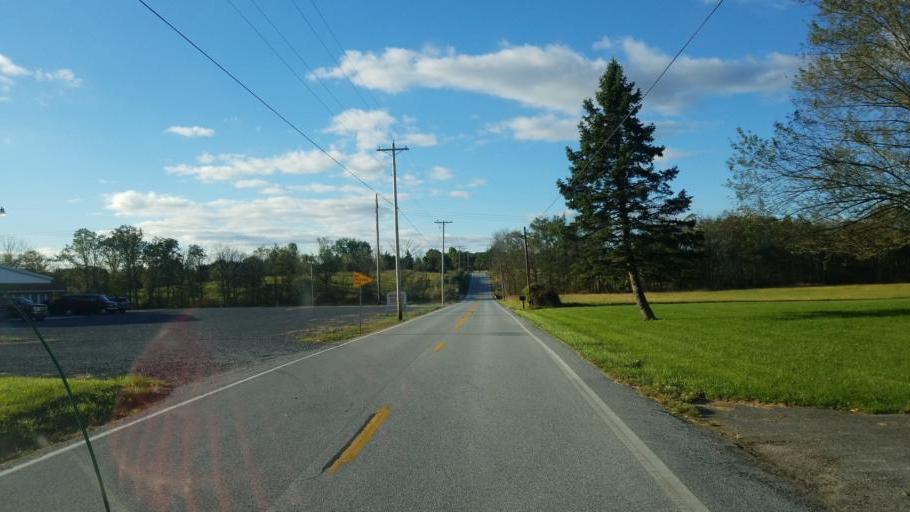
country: US
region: Pennsylvania
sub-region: Adams County
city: Gettysburg
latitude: 39.8775
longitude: -77.2303
